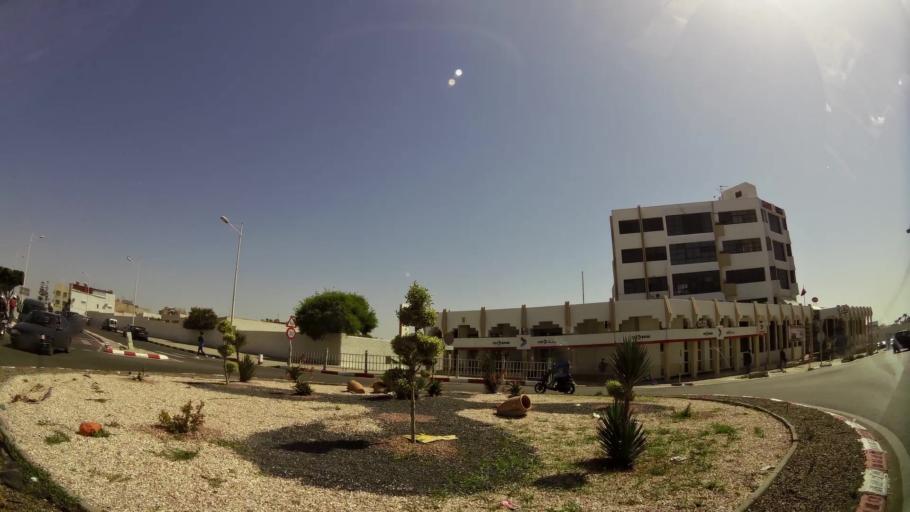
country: MA
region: Souss-Massa-Draa
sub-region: Agadir-Ida-ou-Tnan
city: Agadir
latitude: 30.4248
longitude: -9.5893
